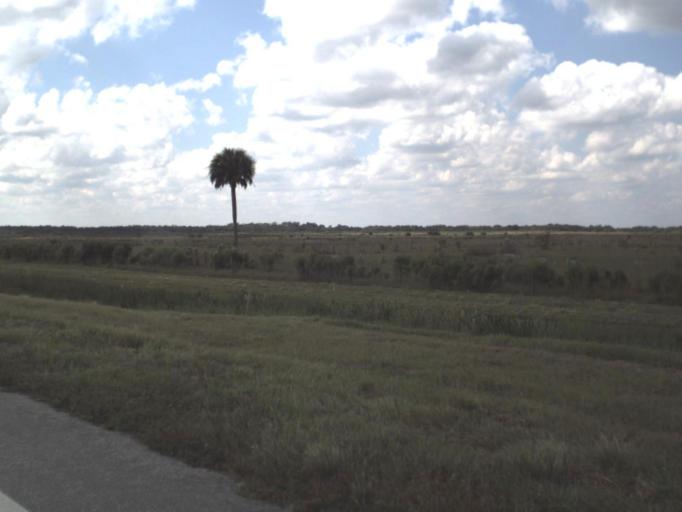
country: US
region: Florida
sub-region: Okeechobee County
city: Okeechobee
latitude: 27.3772
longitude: -81.0432
